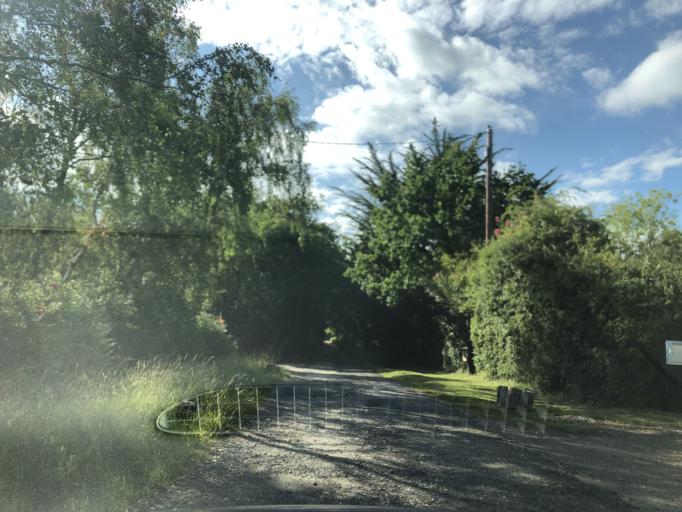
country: GB
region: England
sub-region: Isle of Wight
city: Shalfleet
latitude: 50.7104
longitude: -1.4413
